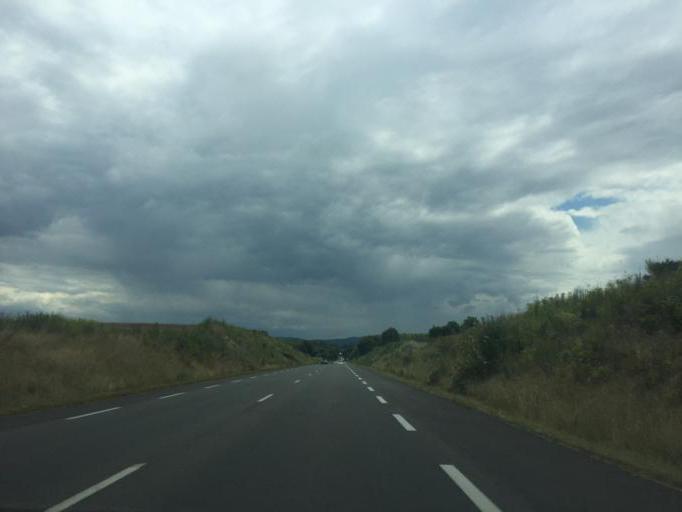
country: FR
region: Rhone-Alpes
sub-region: Departement de l'Isere
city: Janneyrias
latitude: 45.7588
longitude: 5.1291
